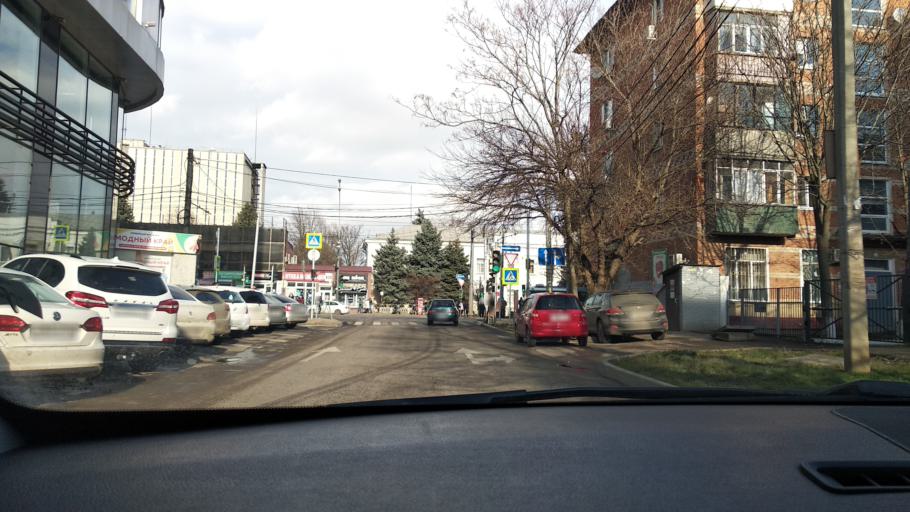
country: RU
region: Krasnodarskiy
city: Krasnodar
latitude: 45.0198
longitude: 39.0044
